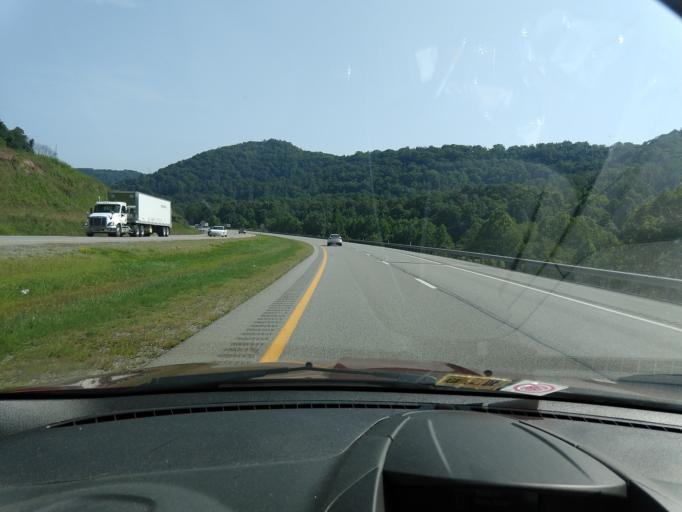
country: US
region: West Virginia
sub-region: Braxton County
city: Sutton
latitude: 38.7869
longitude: -80.6659
